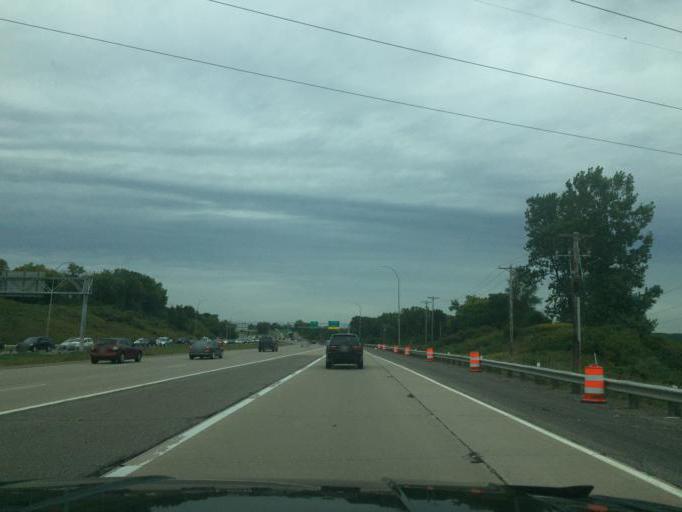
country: US
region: Minnesota
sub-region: Dakota County
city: Mendota Heights
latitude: 44.8648
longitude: -93.2049
